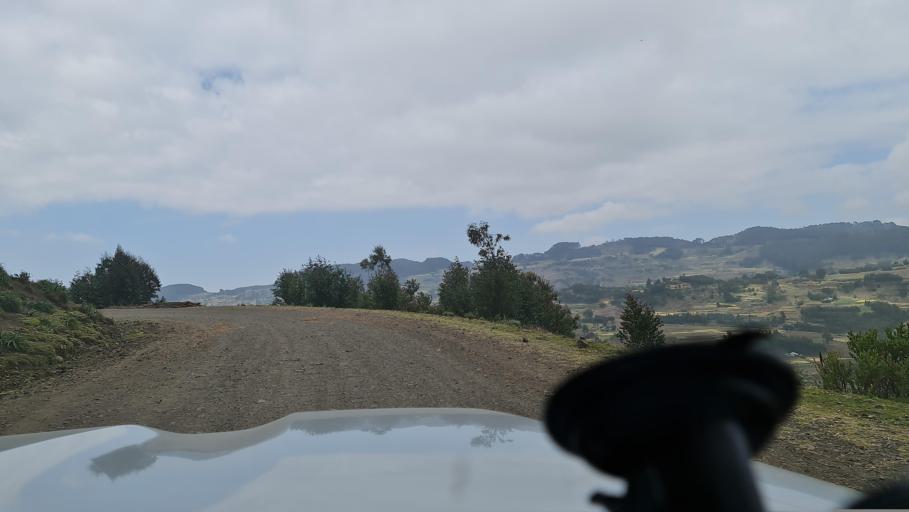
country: ET
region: Amhara
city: Abomsa
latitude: 10.1377
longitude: 39.7898
